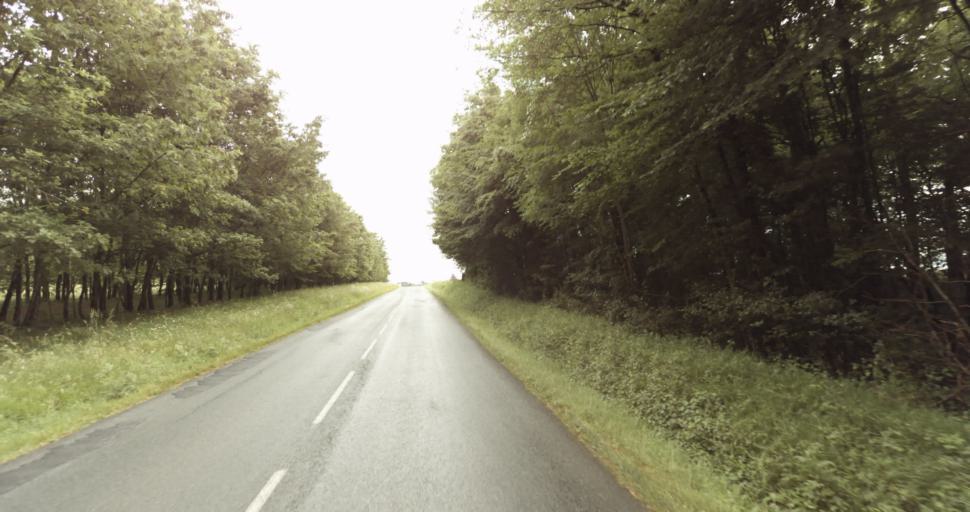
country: FR
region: Aquitaine
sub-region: Departement de la Dordogne
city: Belves
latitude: 44.7002
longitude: 0.9185
